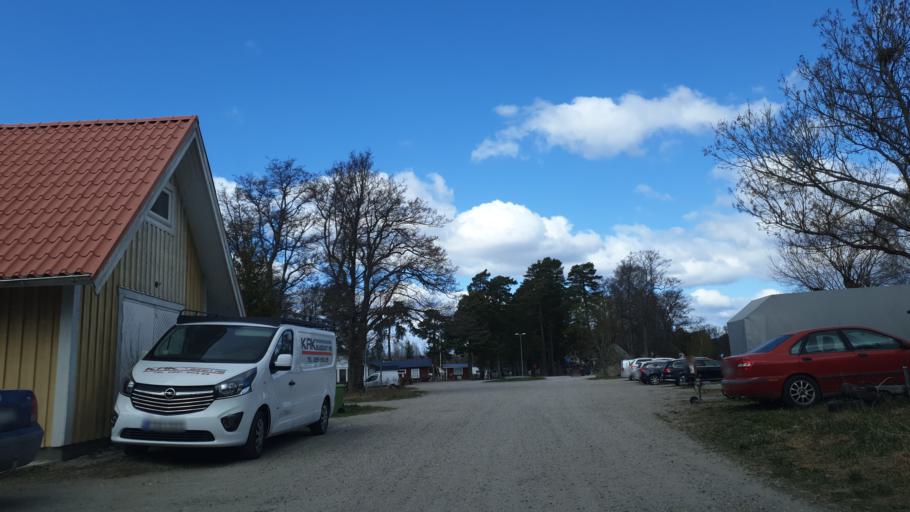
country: SE
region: Vaestmanland
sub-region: Kungsors Kommun
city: Kungsoer
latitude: 59.4728
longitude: 16.0666
